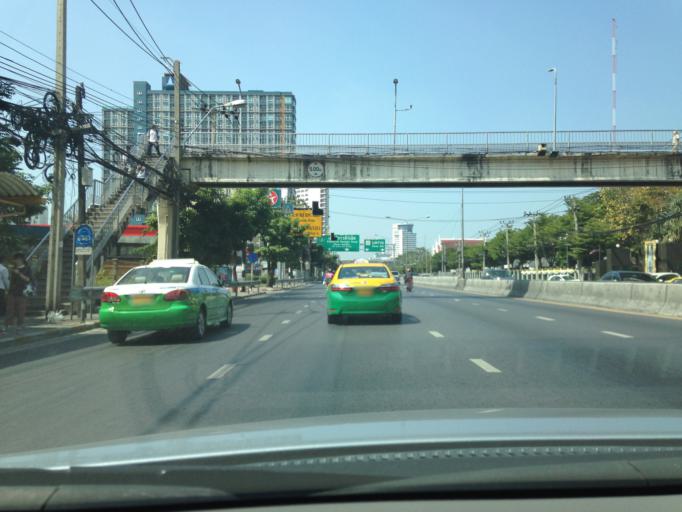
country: TH
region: Bangkok
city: Chatuchak
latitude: 13.8447
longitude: 100.5666
